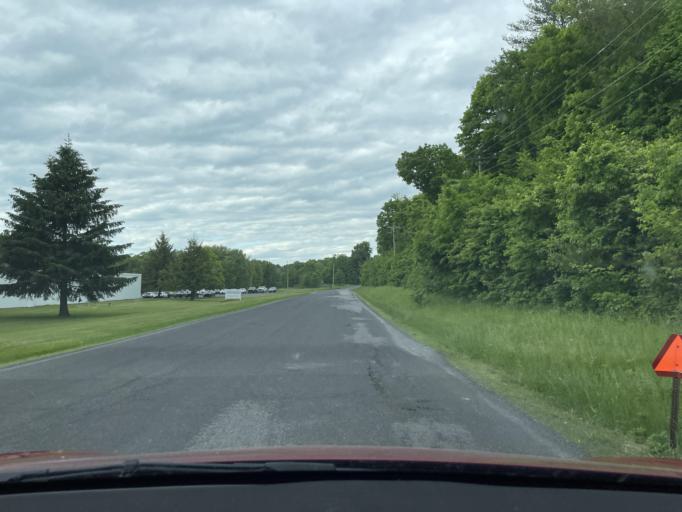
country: US
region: New York
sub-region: Ulster County
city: Saugerties
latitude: 42.0854
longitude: -73.9591
